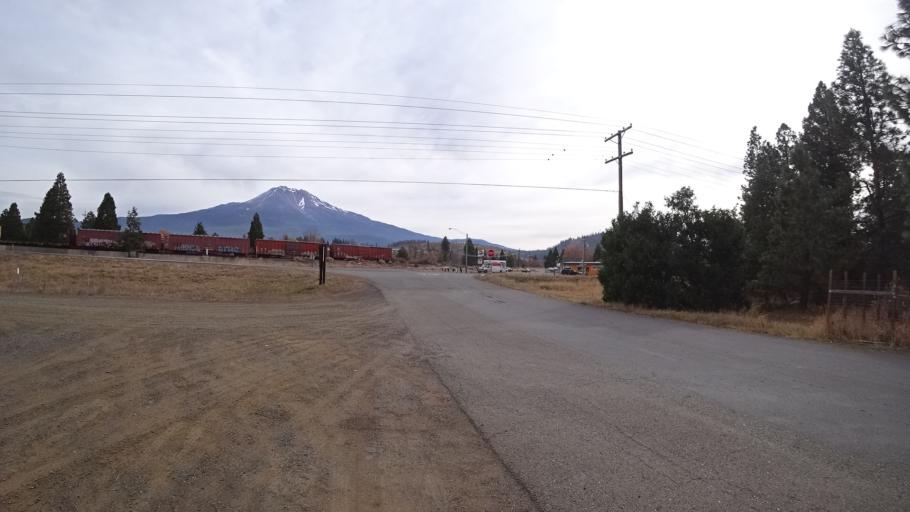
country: US
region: California
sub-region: Siskiyou County
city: Weed
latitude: 41.4308
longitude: -122.3896
